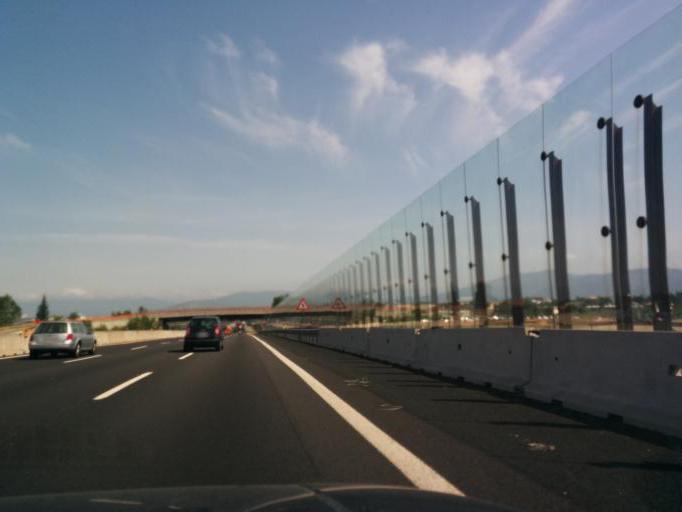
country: IT
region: Tuscany
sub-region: Province of Florence
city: Scandicci
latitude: 43.7537
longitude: 11.1713
